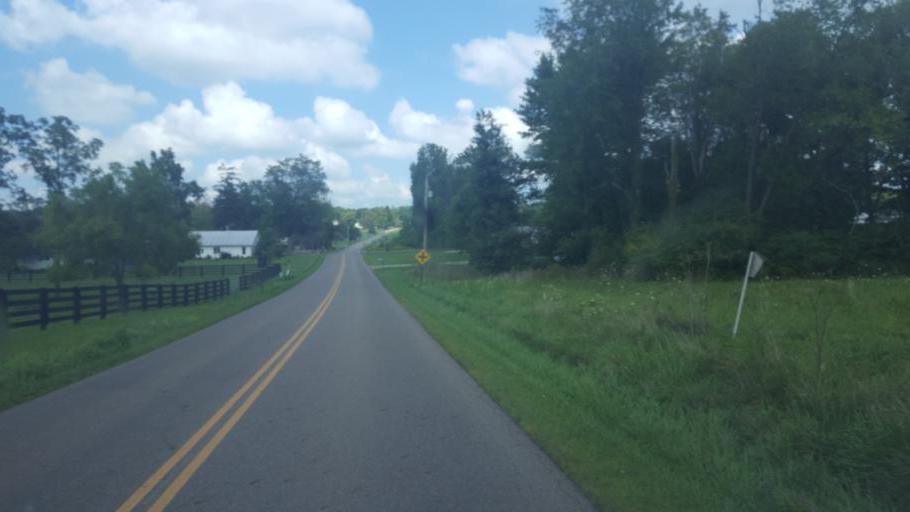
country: US
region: Ohio
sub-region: Knox County
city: Mount Vernon
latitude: 40.4478
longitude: -82.4870
